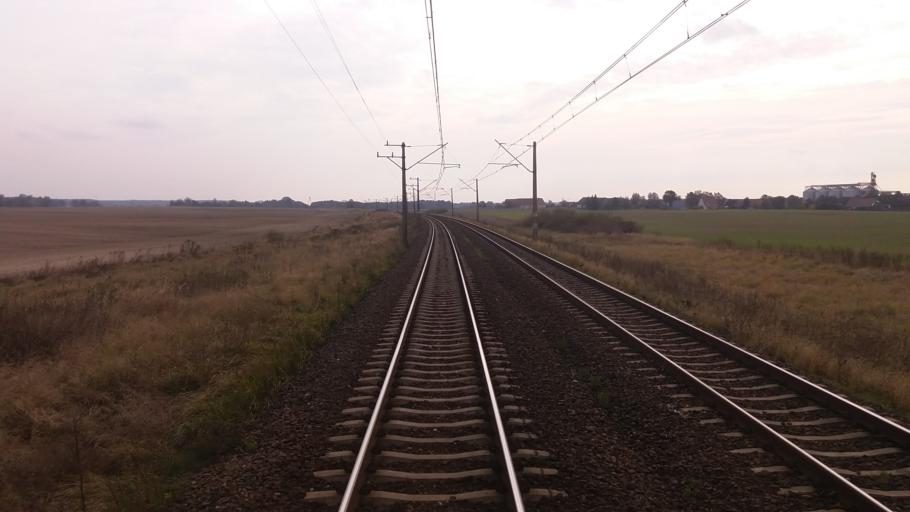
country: PL
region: West Pomeranian Voivodeship
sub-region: Powiat stargardzki
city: Dolice
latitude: 53.2339
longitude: 15.1340
